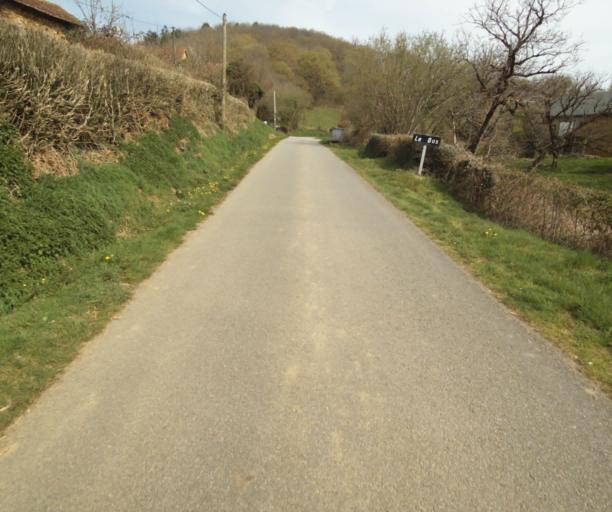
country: FR
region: Limousin
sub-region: Departement de la Correze
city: Naves
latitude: 45.3204
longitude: 1.8019
